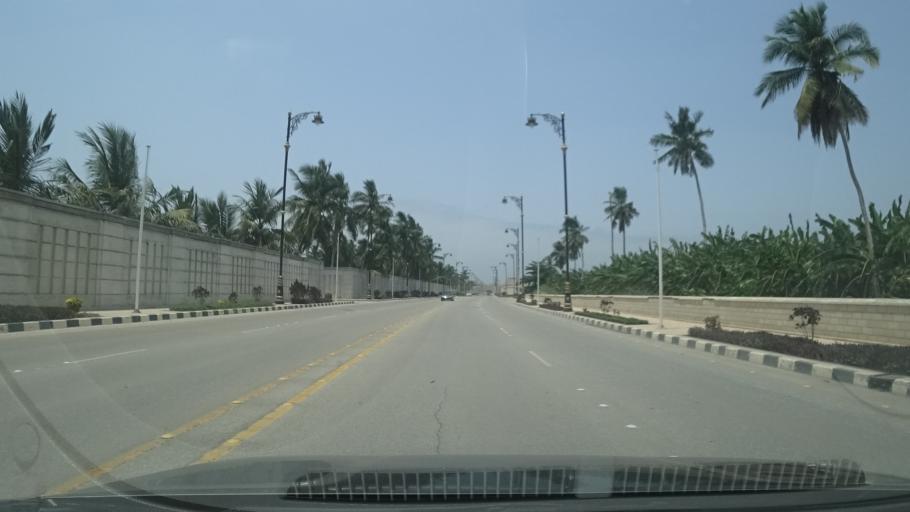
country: OM
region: Zufar
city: Salalah
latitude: 17.0062
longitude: 54.0963
